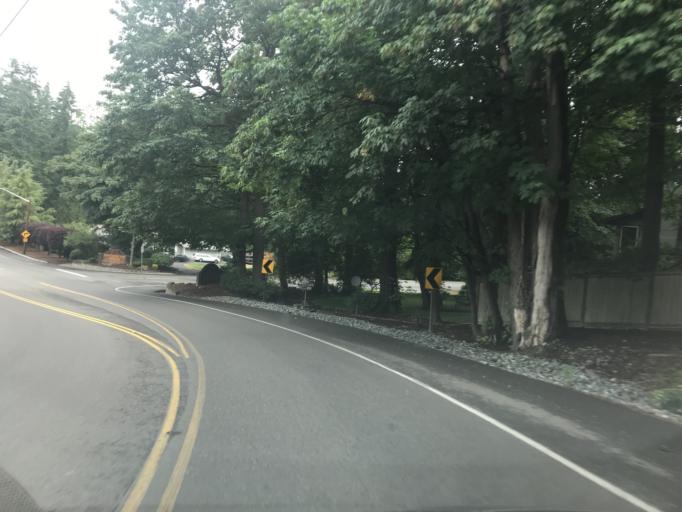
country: US
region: Washington
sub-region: King County
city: Lake Morton-Berrydale
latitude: 47.3436
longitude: -122.0999
